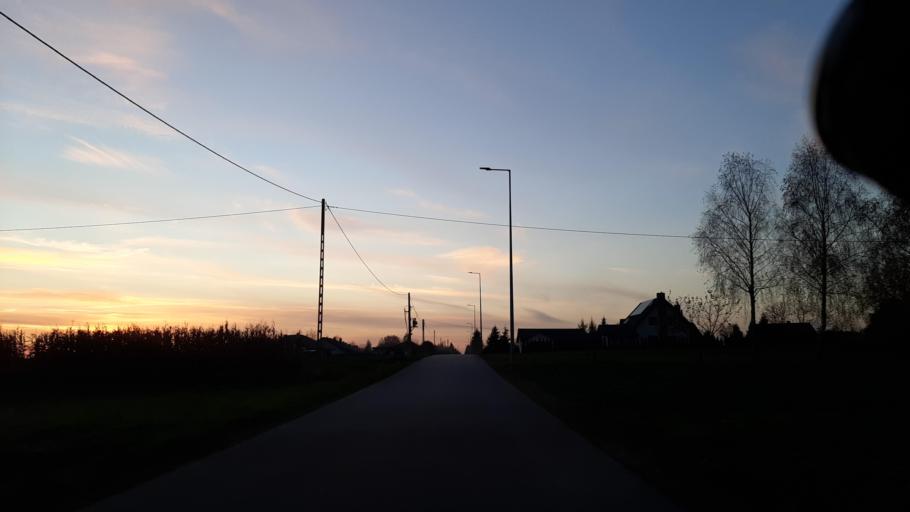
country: PL
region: Lublin Voivodeship
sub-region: Powiat lubelski
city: Jastkow
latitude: 51.3237
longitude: 22.4526
